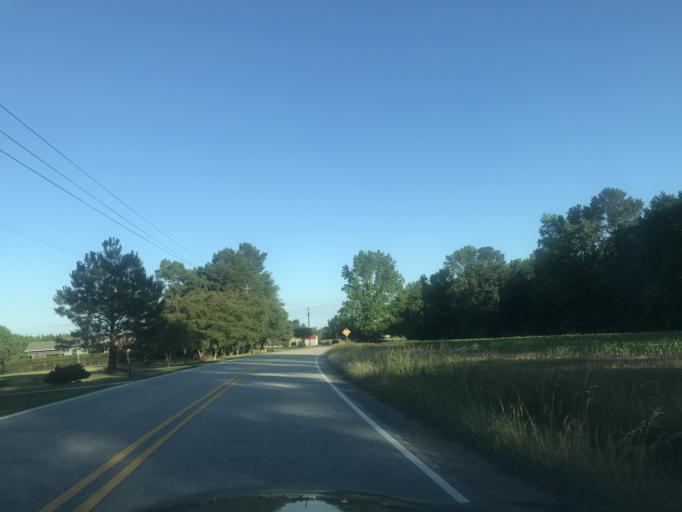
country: US
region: North Carolina
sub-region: Johnston County
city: Archer Lodge
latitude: 35.6990
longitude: -78.3791
